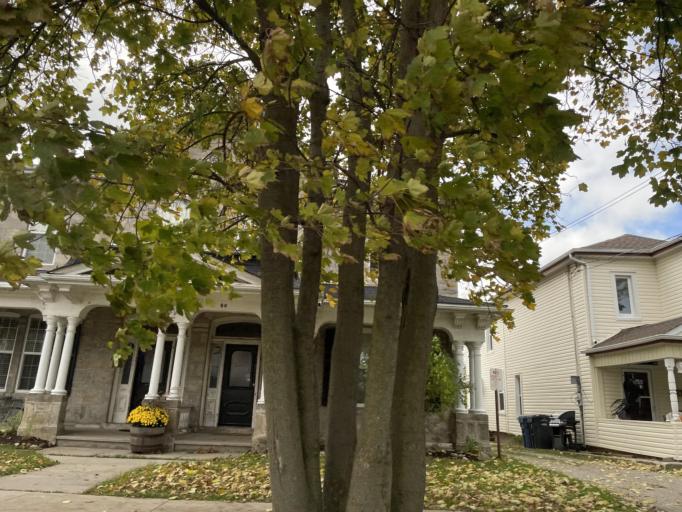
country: CA
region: Ontario
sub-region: Wellington County
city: Guelph
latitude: 43.5436
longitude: -80.2534
